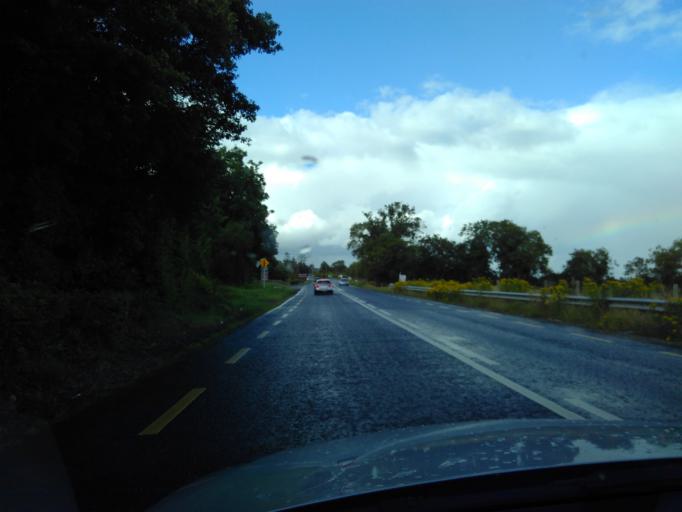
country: IE
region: Ulster
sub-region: County Donegal
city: Ramelton
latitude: 54.9831
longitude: -7.6732
